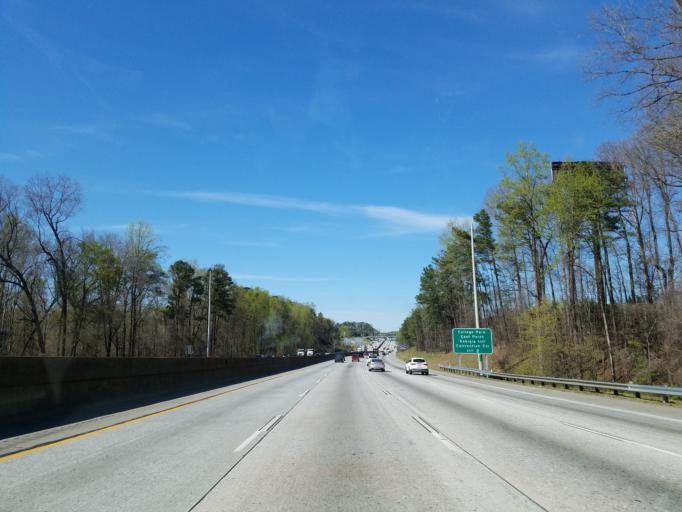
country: US
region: Georgia
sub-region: Fulton County
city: College Park
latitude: 33.6474
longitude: -84.4974
